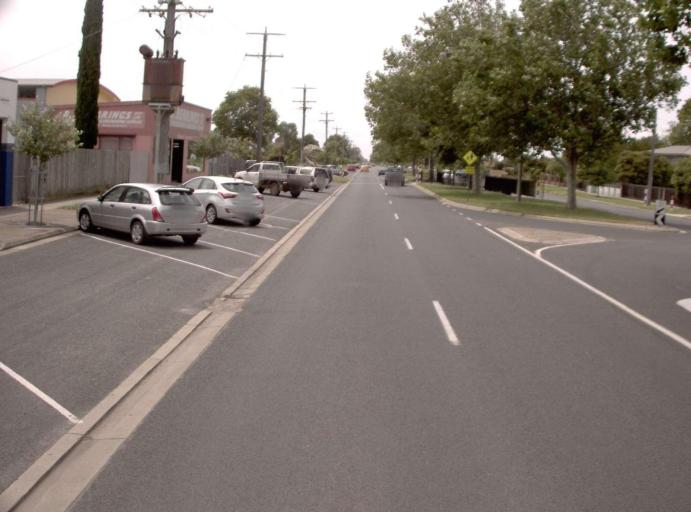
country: AU
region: Victoria
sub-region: Wellington
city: Sale
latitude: -38.0988
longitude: 147.0717
